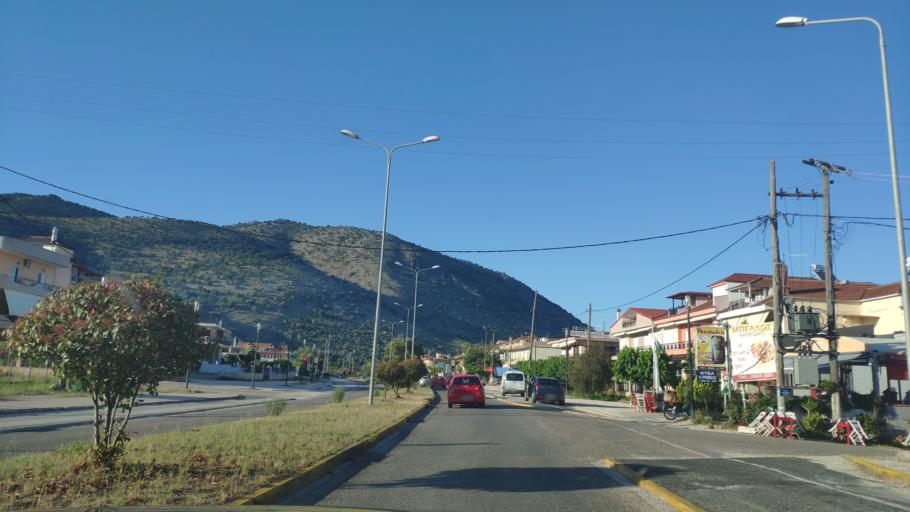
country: GR
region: Epirus
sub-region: Nomos Prevezis
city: Louros
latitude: 39.1674
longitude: 20.7585
